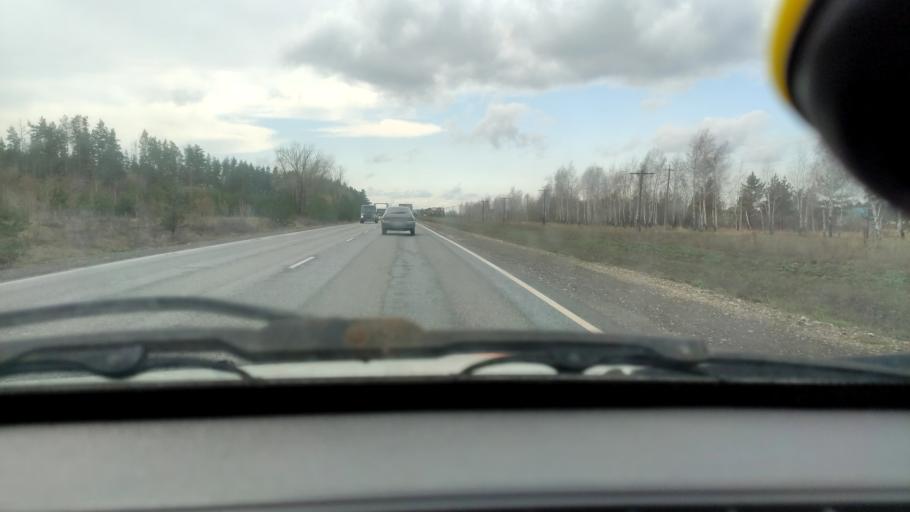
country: RU
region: Samara
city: Povolzhskiy
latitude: 53.5967
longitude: 49.5883
